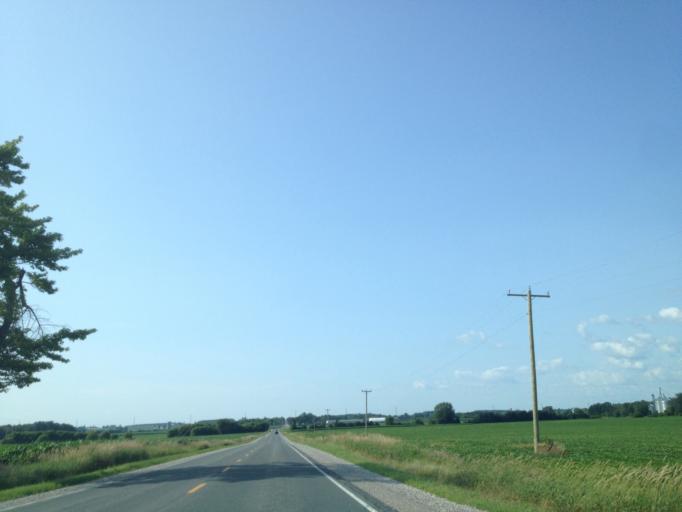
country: CA
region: Ontario
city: Aylmer
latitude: 42.8387
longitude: -80.8335
